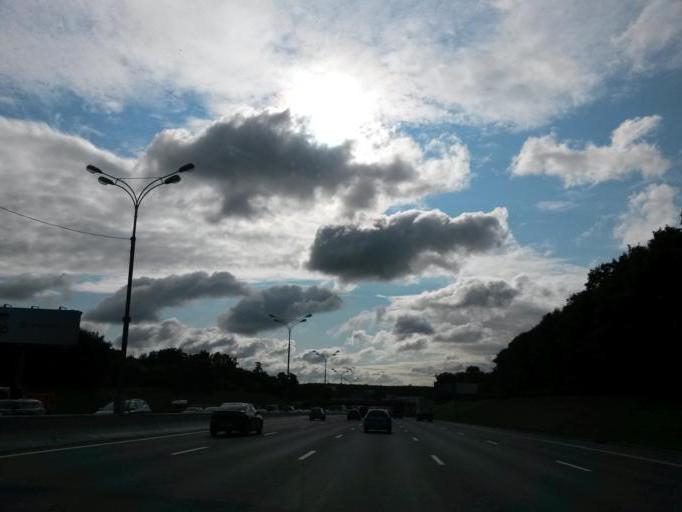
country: RU
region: Moscow
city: Zagor'ye
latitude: 55.5723
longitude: 37.6582
